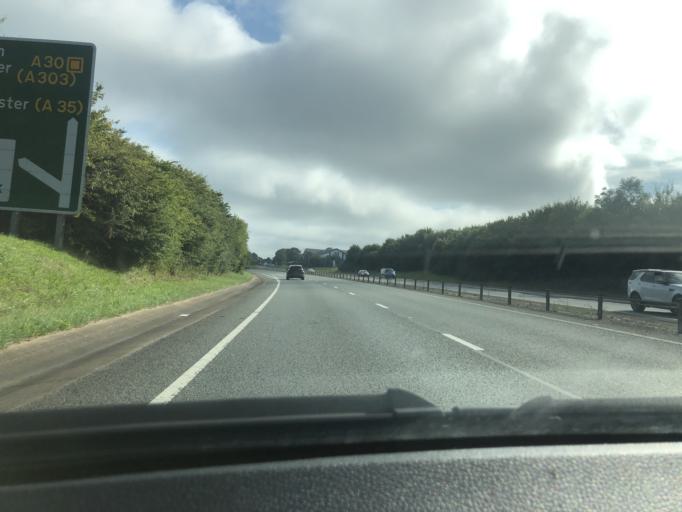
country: GB
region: England
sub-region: Devon
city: Honiton
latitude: 50.7925
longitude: -3.2138
